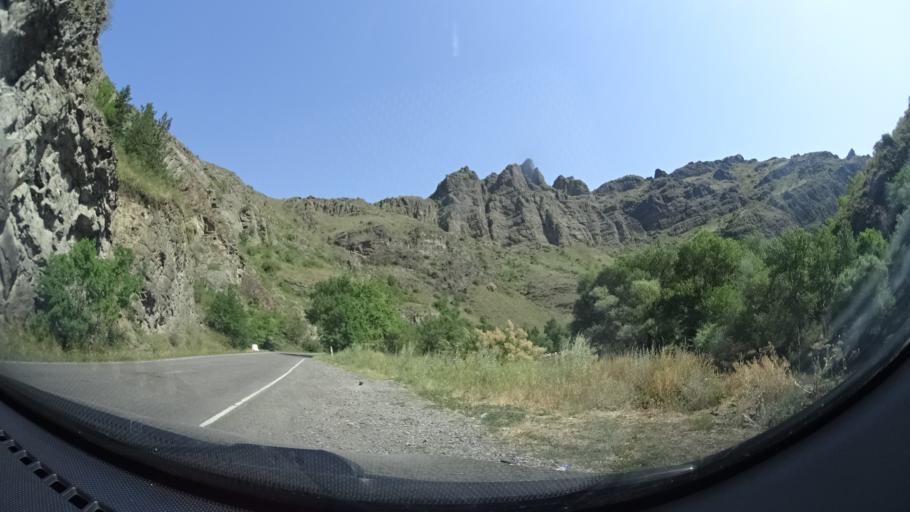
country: GE
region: Samtskhe-Javakheti
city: Akhaltsikhe
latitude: 41.6104
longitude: 43.0687
